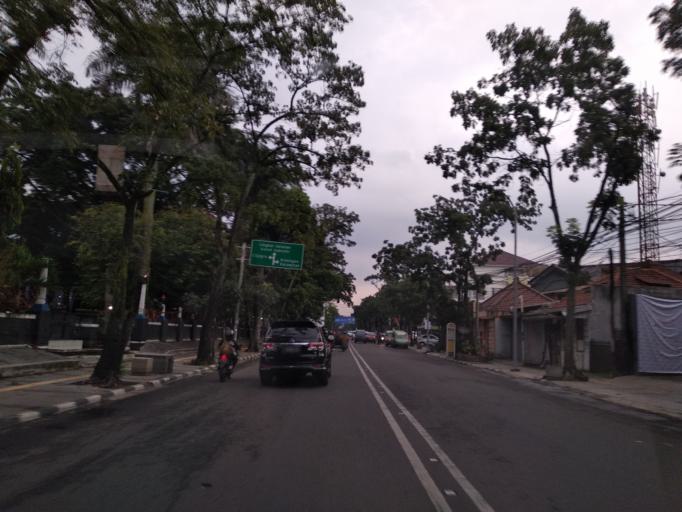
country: ID
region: West Java
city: Bandung
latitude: -6.9430
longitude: 107.6285
